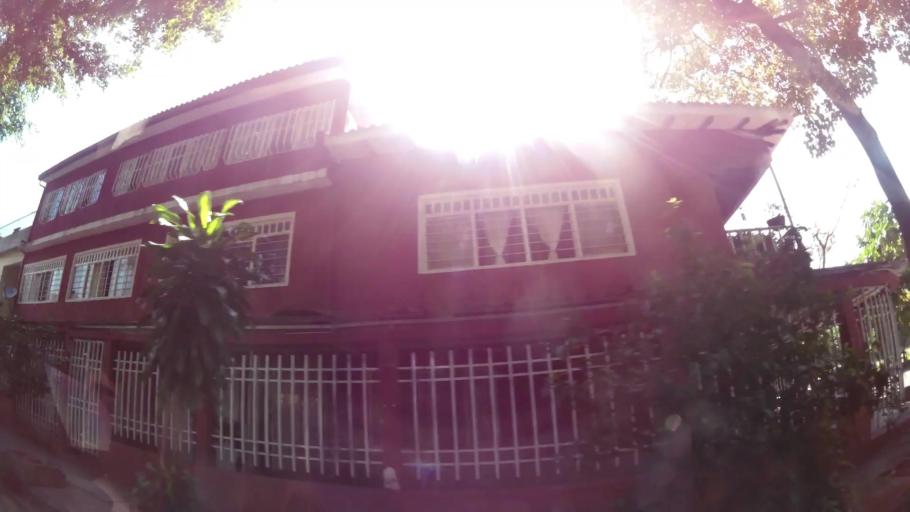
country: CO
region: Valle del Cauca
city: Cali
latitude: 3.4225
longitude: -76.5320
